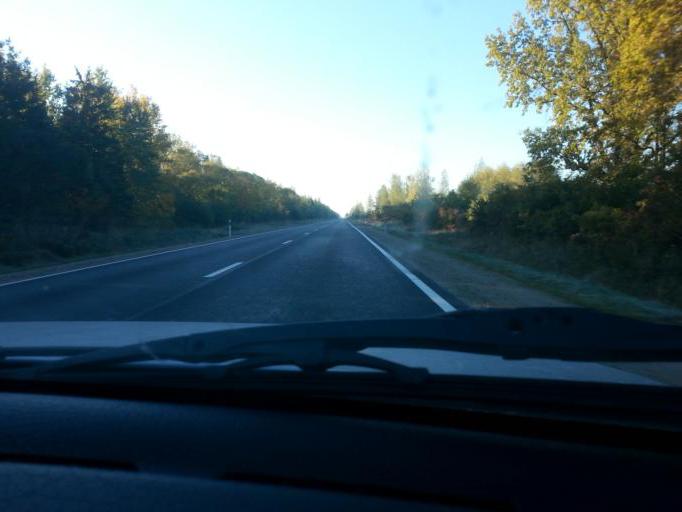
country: LV
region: Jelgava
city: Jelgava
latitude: 56.4972
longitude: 23.6992
